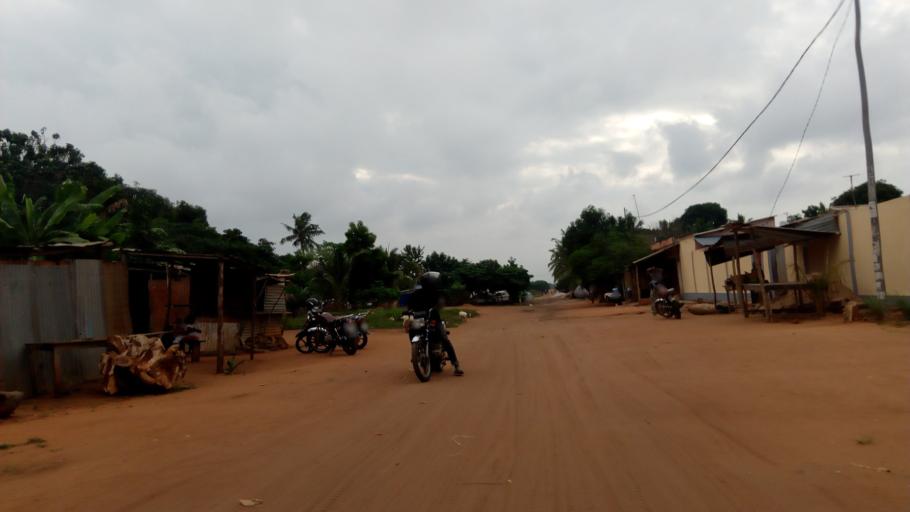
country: TG
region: Maritime
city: Lome
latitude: 6.1731
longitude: 1.1952
